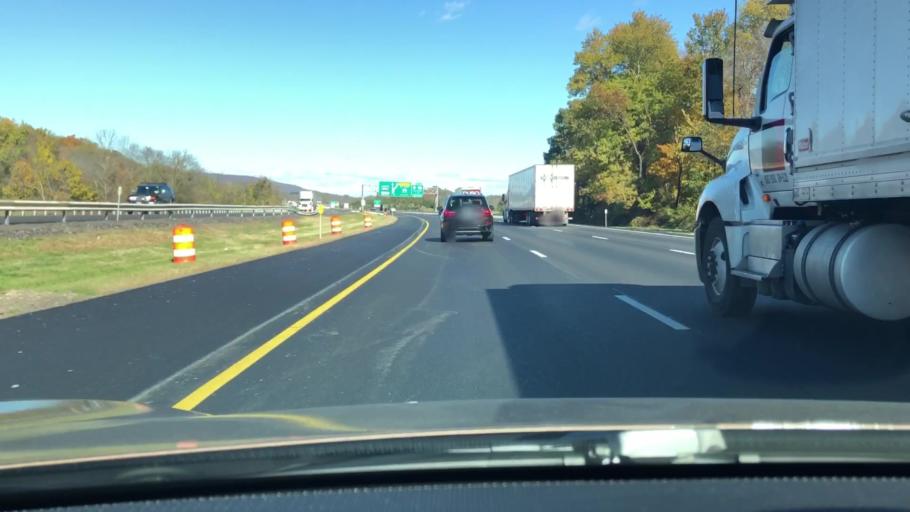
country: US
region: New York
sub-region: Orange County
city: Harriman
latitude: 41.2842
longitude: -74.1419
